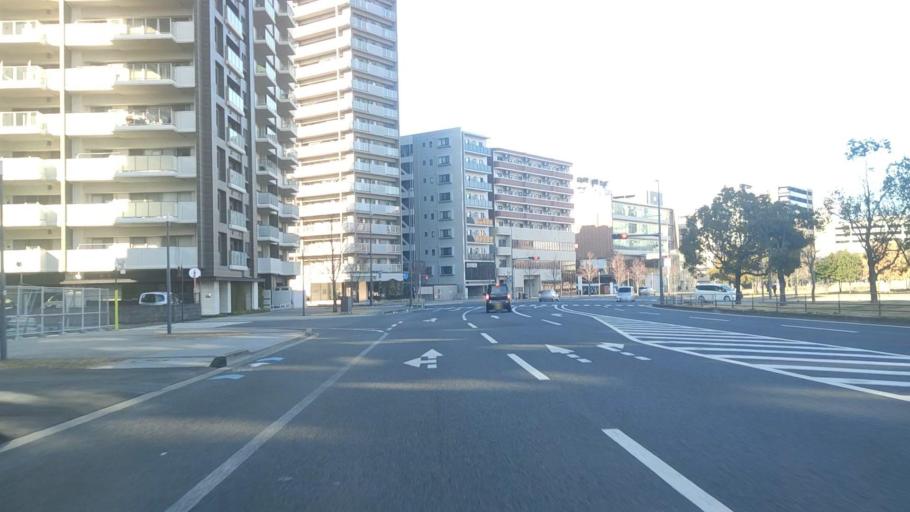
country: JP
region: Oita
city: Oita
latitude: 33.2289
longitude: 131.6034
